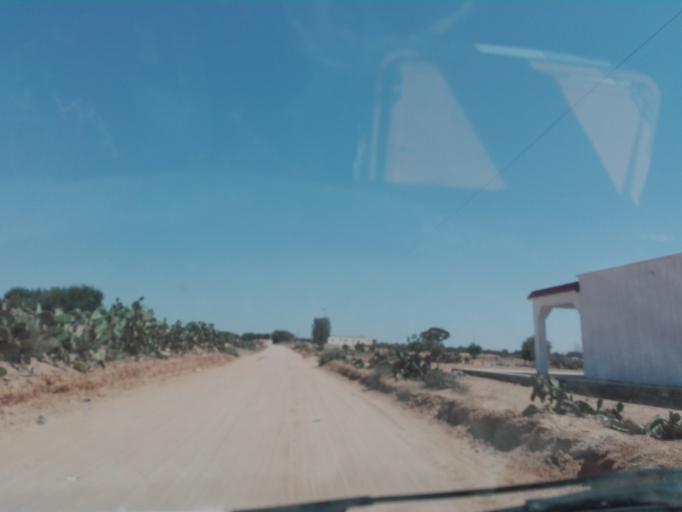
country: TN
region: Safaqis
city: Bi'r `Ali Bin Khalifah
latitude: 34.6615
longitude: 10.2403
